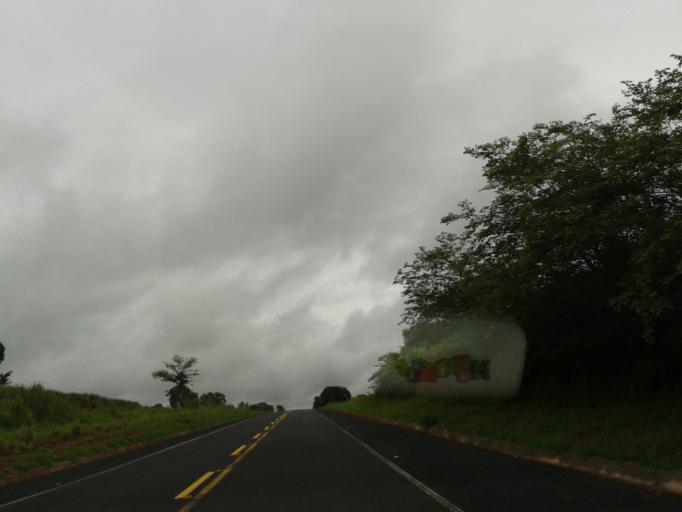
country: BR
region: Minas Gerais
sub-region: Santa Vitoria
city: Santa Vitoria
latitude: -19.2340
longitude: -50.0171
